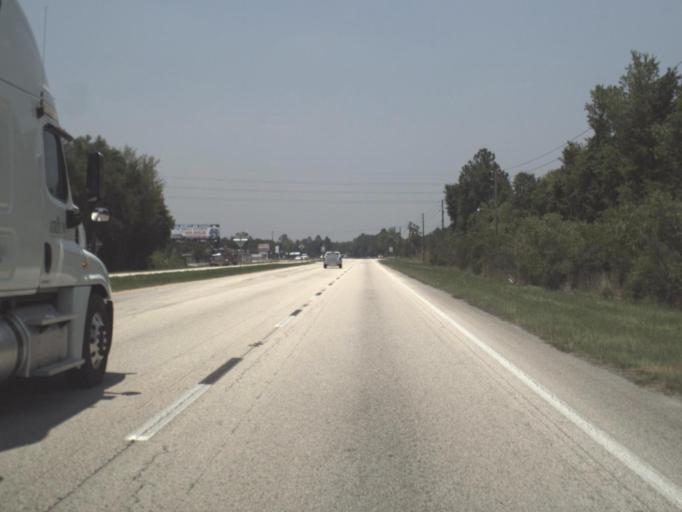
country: US
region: Florida
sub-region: Bradford County
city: Starke
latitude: 30.0518
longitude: -82.0691
